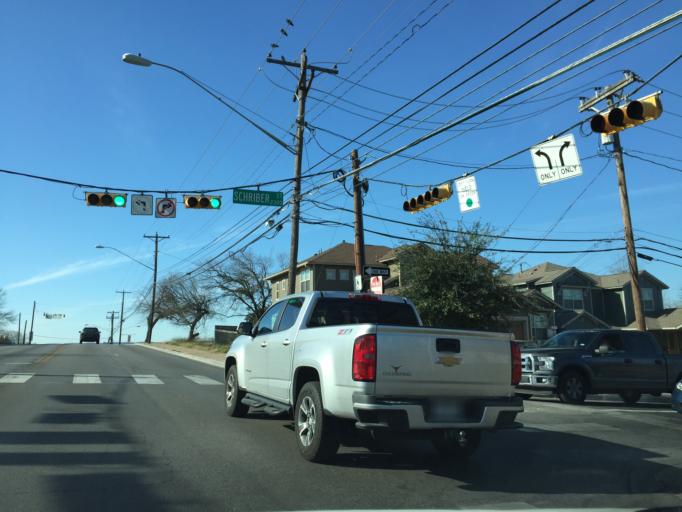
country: US
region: Texas
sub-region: Travis County
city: Austin
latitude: 30.2346
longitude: -97.7436
